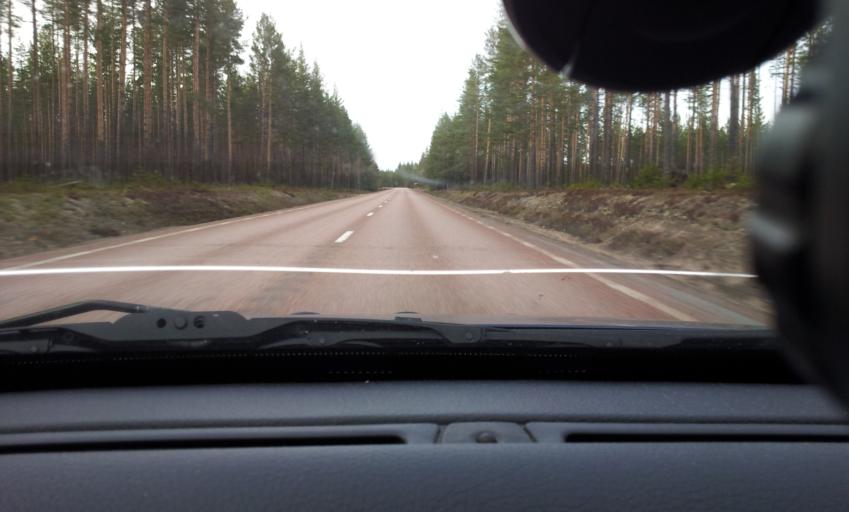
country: SE
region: Gaevleborg
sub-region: Ljusdals Kommun
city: Farila
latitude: 61.8432
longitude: 15.7506
